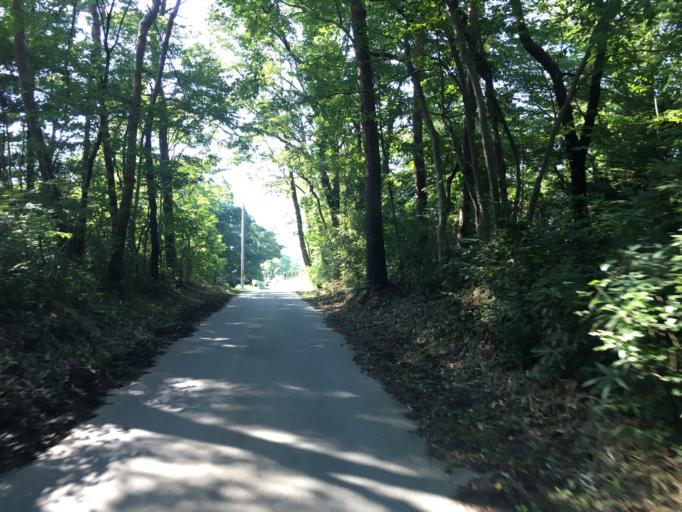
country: JP
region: Miyagi
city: Marumori
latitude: 37.8230
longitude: 140.8991
